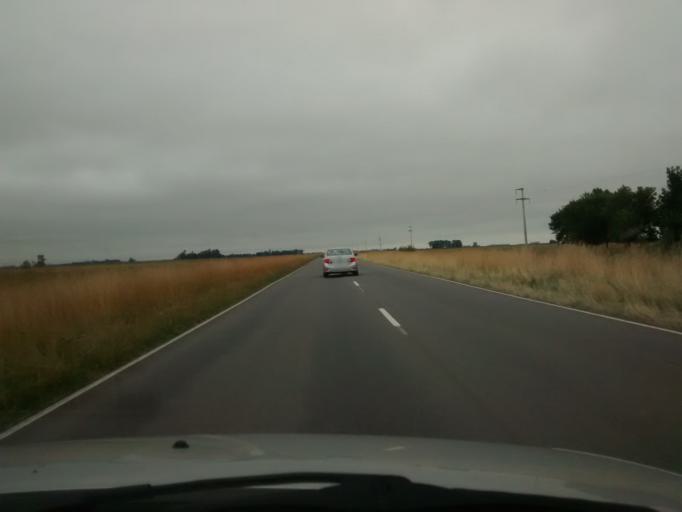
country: AR
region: Buenos Aires
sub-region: Partido de Ayacucho
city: Ayacucho
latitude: -37.0298
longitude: -58.5396
